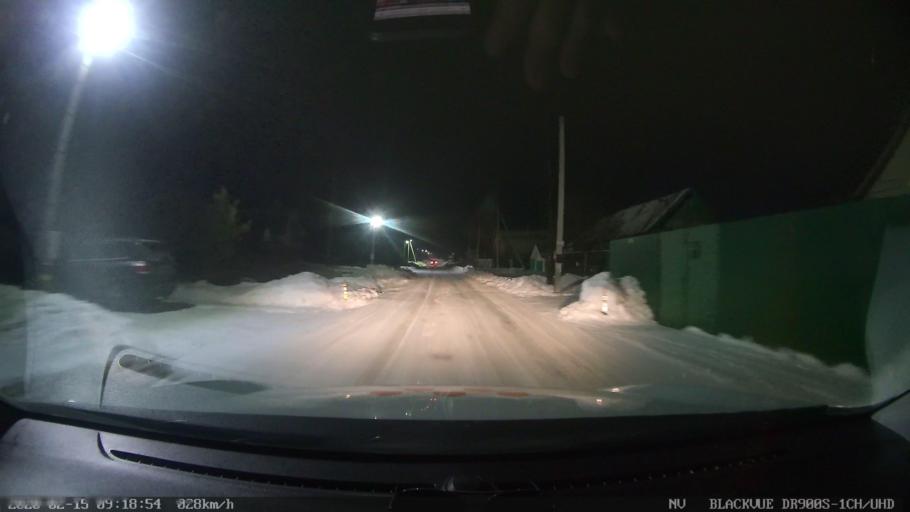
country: RU
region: Tatarstan
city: Stolbishchi
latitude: 55.7162
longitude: 49.3622
